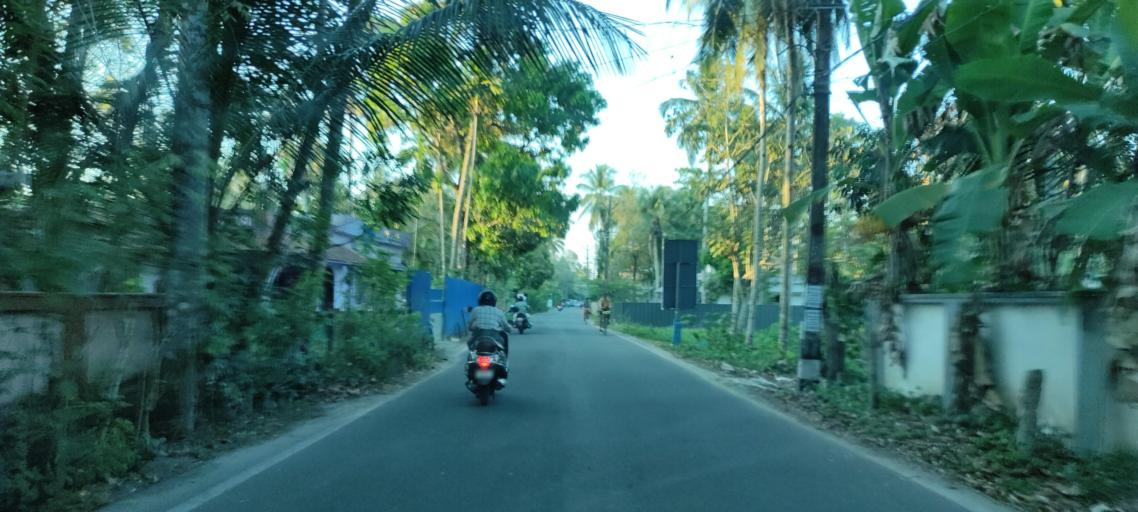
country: IN
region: Kerala
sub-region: Alappuzha
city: Kayankulam
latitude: 9.2051
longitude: 76.4627
